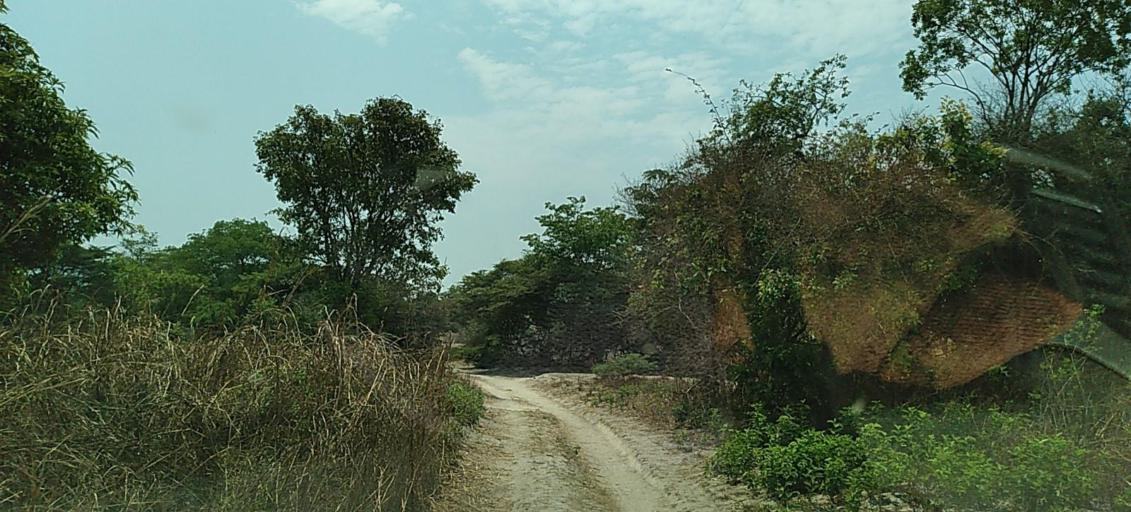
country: ZM
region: Copperbelt
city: Kalulushi
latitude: -12.9439
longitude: 28.1235
